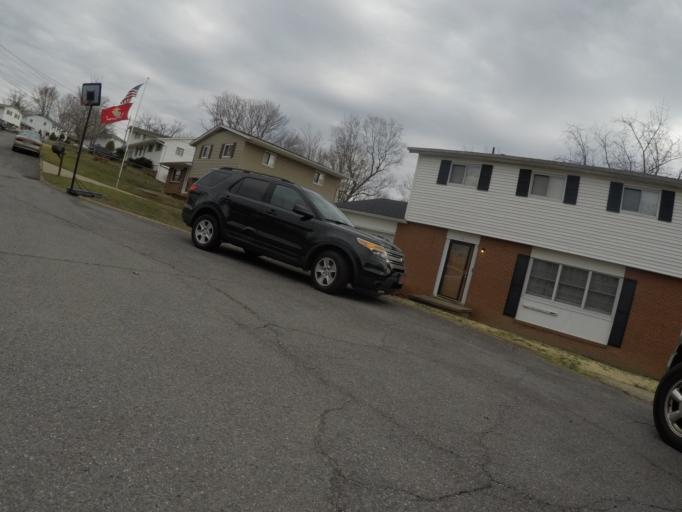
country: US
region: West Virginia
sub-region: Cabell County
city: Pea Ridge
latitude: 38.3916
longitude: -82.3792
